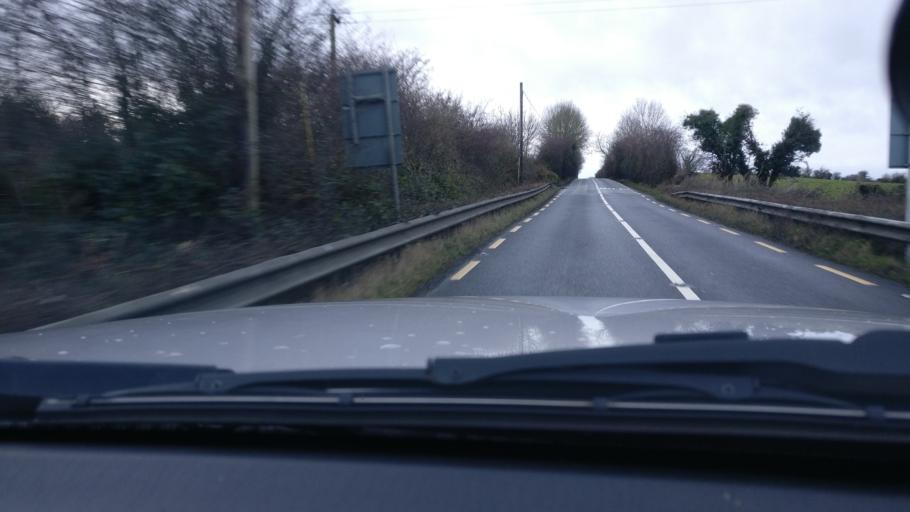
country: IE
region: Leinster
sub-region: An Iarmhi
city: Moate
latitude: 53.5827
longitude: -7.7309
